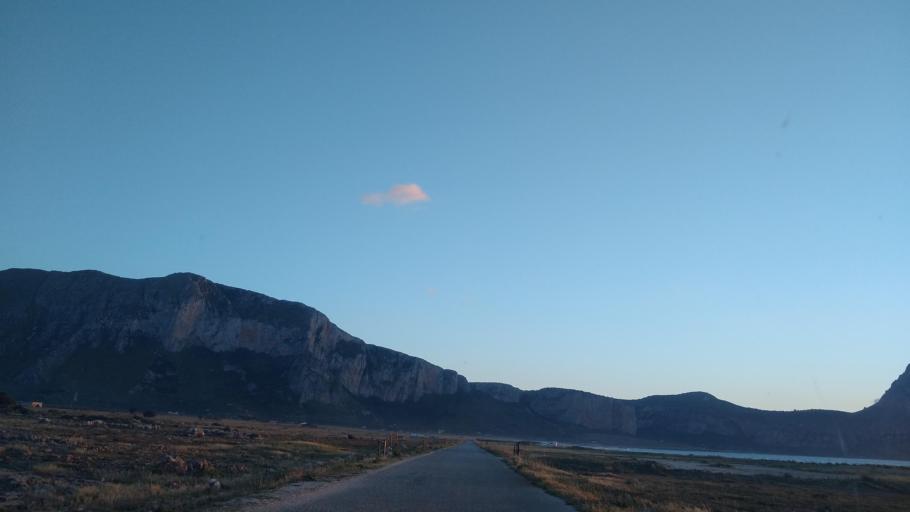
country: IT
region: Sicily
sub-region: Trapani
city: Castelluzzo
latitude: 38.1228
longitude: 12.7259
